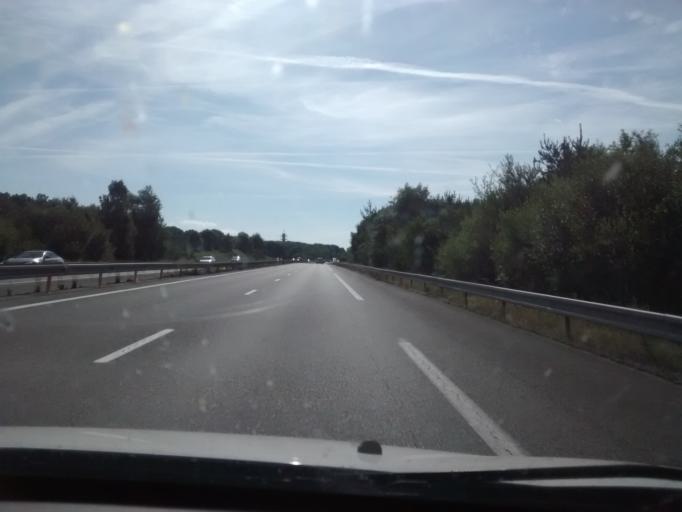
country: FR
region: Pays de la Loire
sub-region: Departement de la Mayenne
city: Port-Brillet
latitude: 48.0773
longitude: -0.9773
